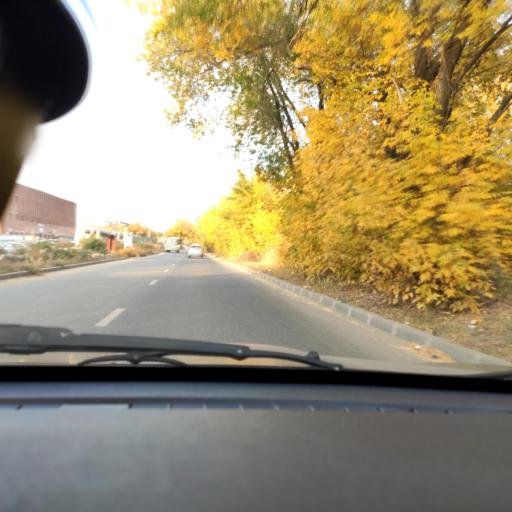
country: RU
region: Samara
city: Tol'yatti
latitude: 53.5604
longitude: 49.3219
